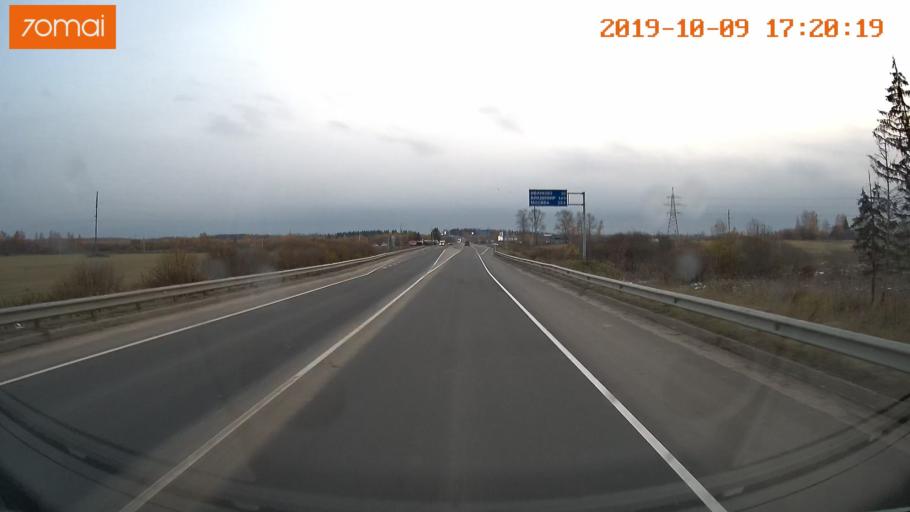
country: RU
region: Ivanovo
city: Furmanov
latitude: 57.2359
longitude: 41.1427
